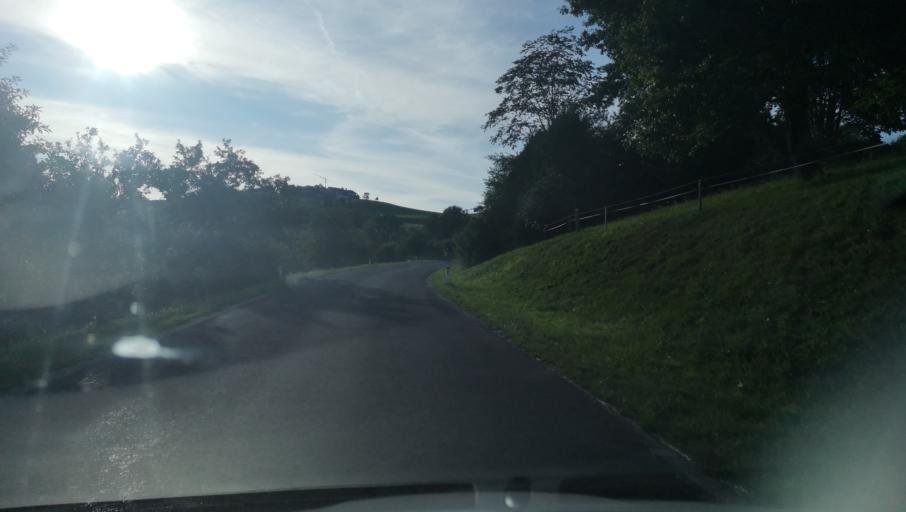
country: AT
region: Lower Austria
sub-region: Waidhofen an der Ybbs Stadt
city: Waidhofen an der Ybbs
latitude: 47.9767
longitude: 14.8158
